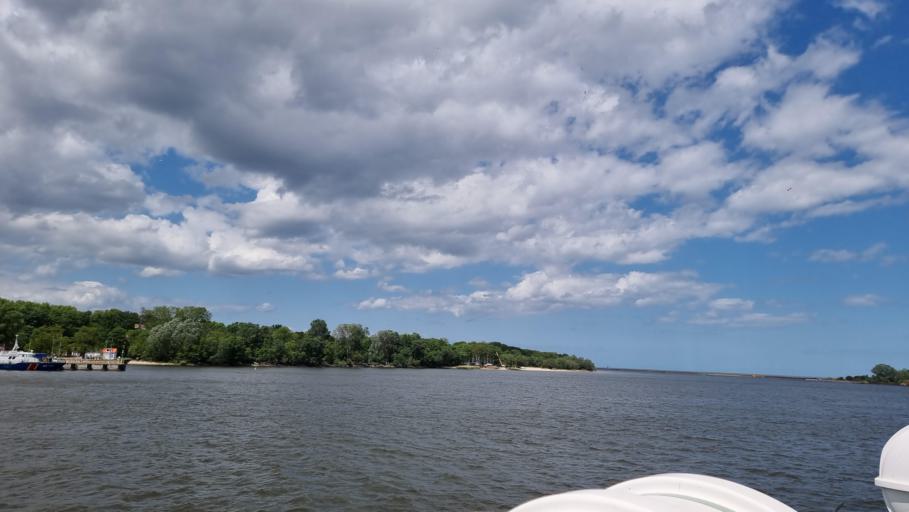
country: PL
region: West Pomeranian Voivodeship
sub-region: Swinoujscie
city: Swinoujscie
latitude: 53.9113
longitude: 14.2770
